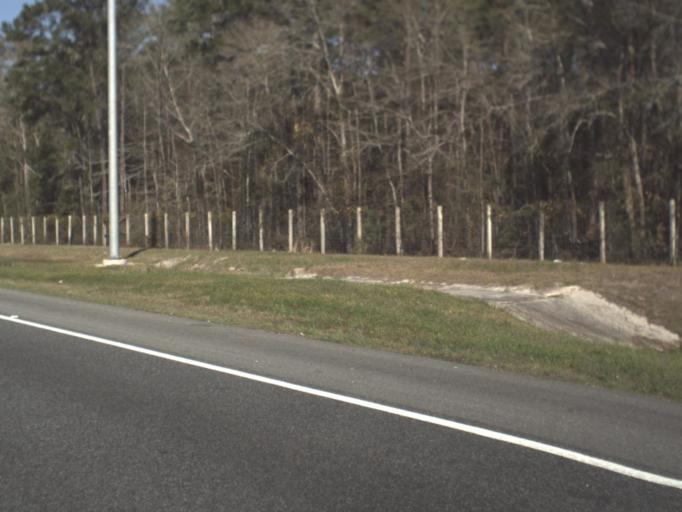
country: US
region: Florida
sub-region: Leon County
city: Tallahassee
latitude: 30.4785
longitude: -84.3554
